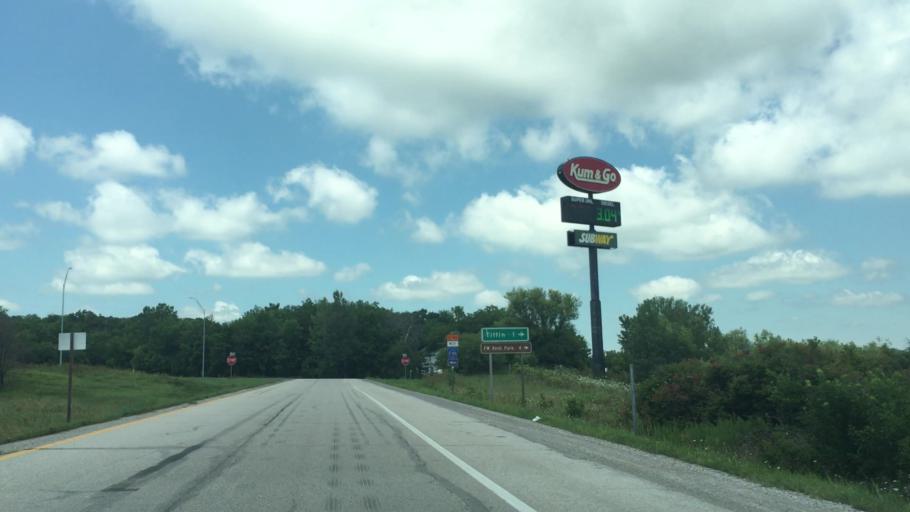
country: US
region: Iowa
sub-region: Johnson County
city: Tiffin
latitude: 41.6948
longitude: -91.6650
